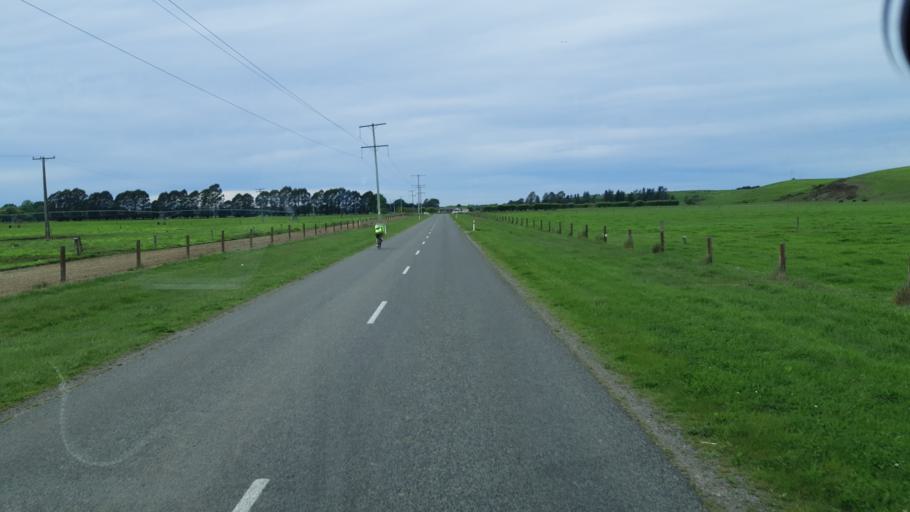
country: NZ
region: Canterbury
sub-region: Timaru District
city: Timaru
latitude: -44.4756
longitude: 171.1395
